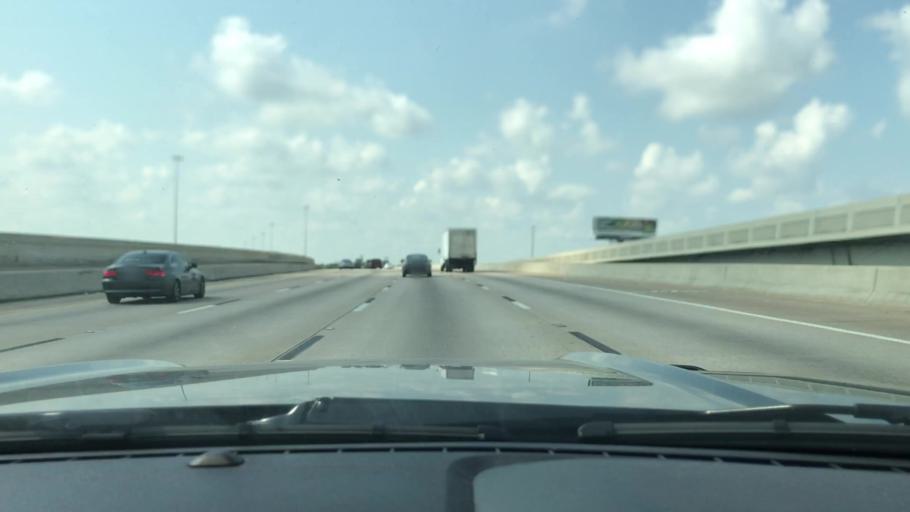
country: US
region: Texas
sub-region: Harris County
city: Aldine
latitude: 29.8657
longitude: -95.3328
